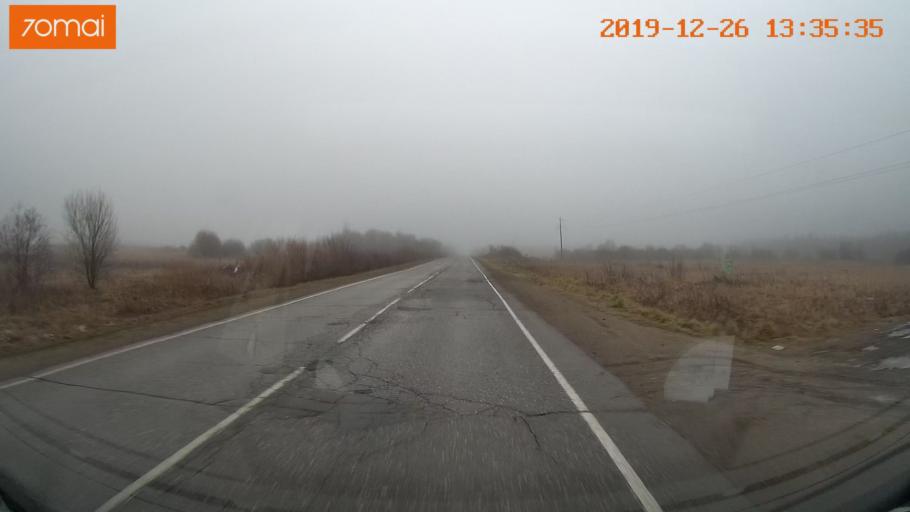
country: RU
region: Vologda
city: Sheksna
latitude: 58.7926
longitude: 38.3415
